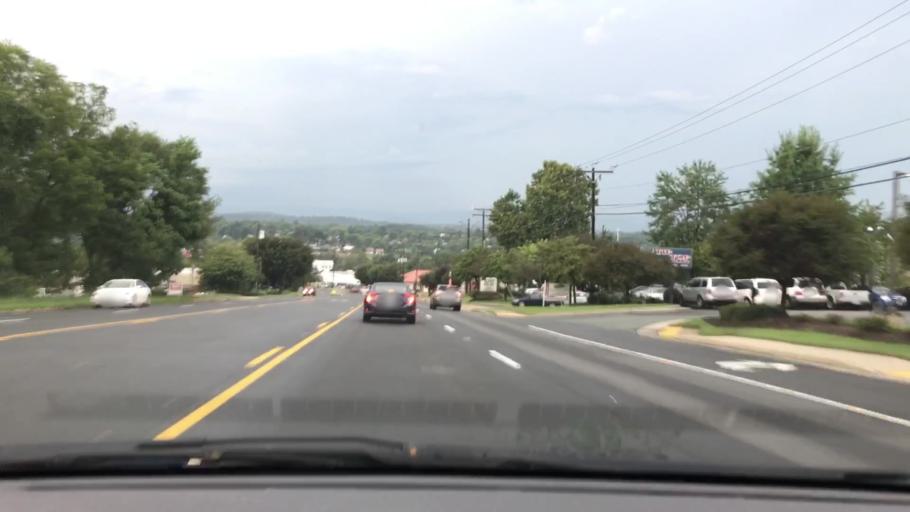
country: US
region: Virginia
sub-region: City of Charlottesville
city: Charlottesville
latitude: 38.0322
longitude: -78.4469
